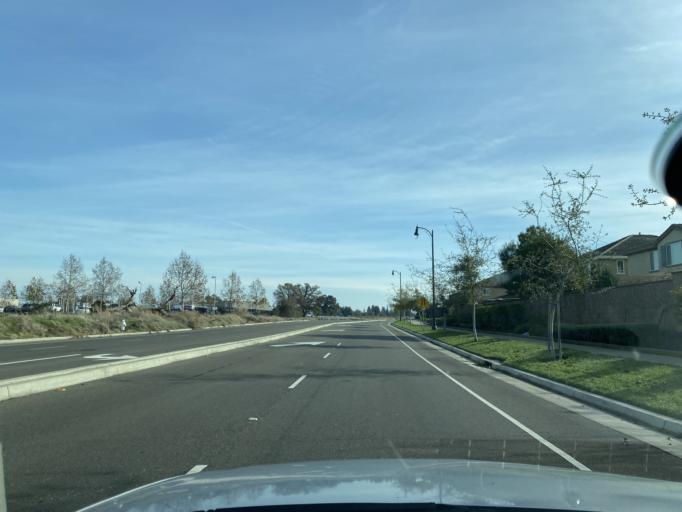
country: US
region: California
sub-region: Sacramento County
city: Elk Grove
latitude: 38.4014
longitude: -121.3911
